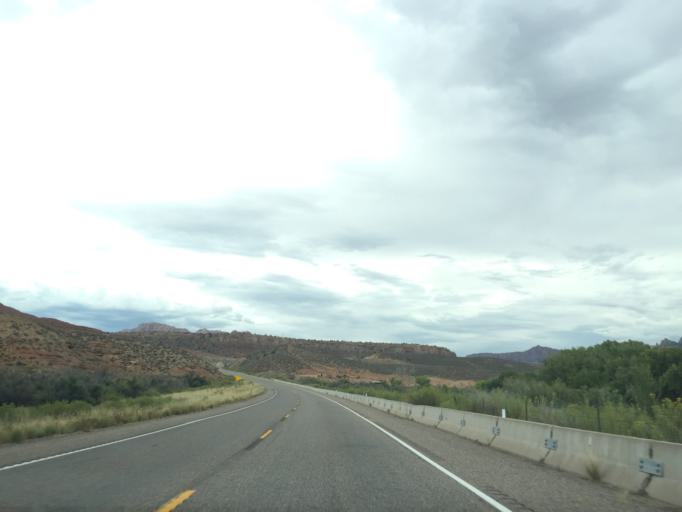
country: US
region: Utah
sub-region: Washington County
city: LaVerkin
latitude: 37.1703
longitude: -113.0804
